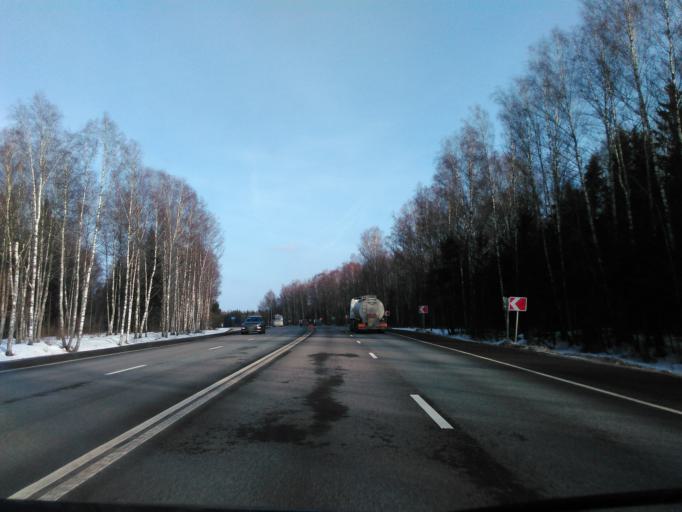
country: RU
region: Smolensk
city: Vyaz'ma
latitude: 55.1874
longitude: 34.0562
